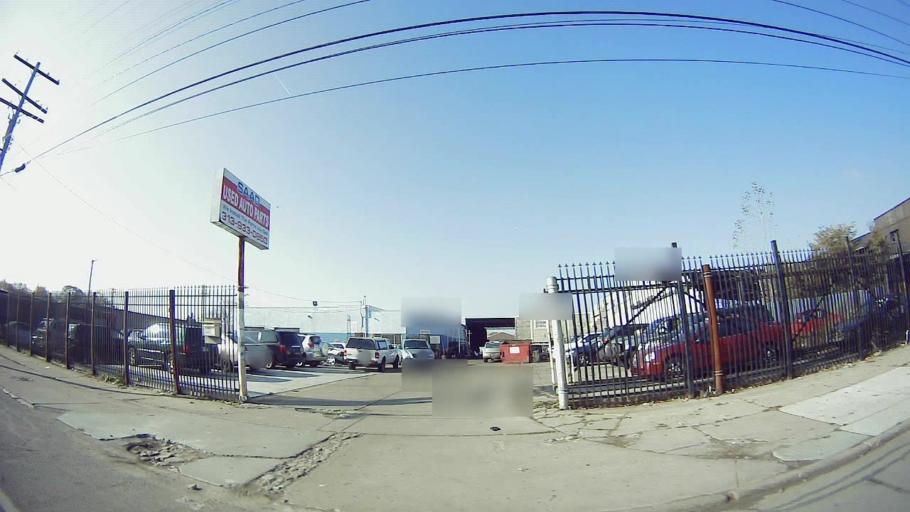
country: US
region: Michigan
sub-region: Wayne County
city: Dearborn
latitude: 42.3722
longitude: -83.1780
